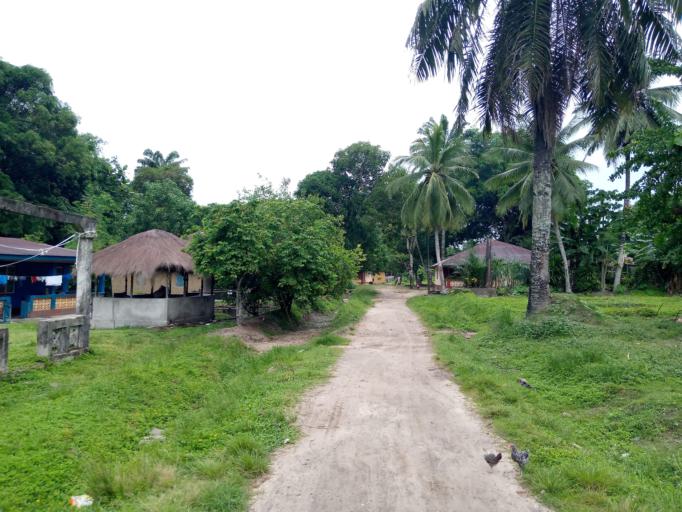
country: SL
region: Southern Province
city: Bonthe
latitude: 7.5320
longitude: -12.5067
